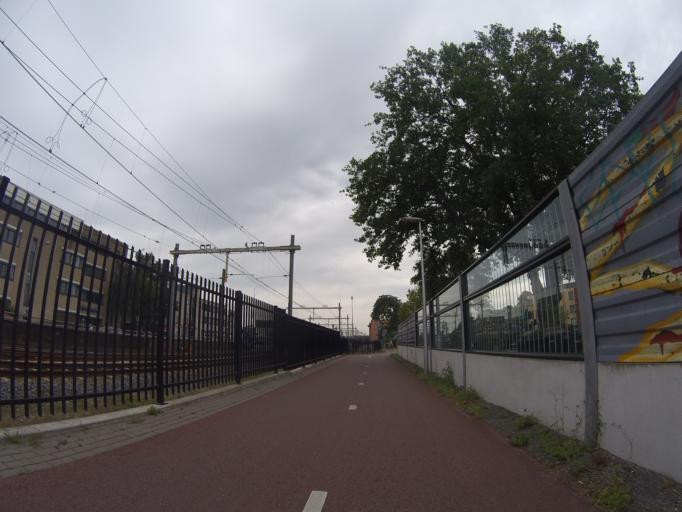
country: NL
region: North Holland
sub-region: Gemeente Hilversum
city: Hilversum
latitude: 52.2295
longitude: 5.1789
